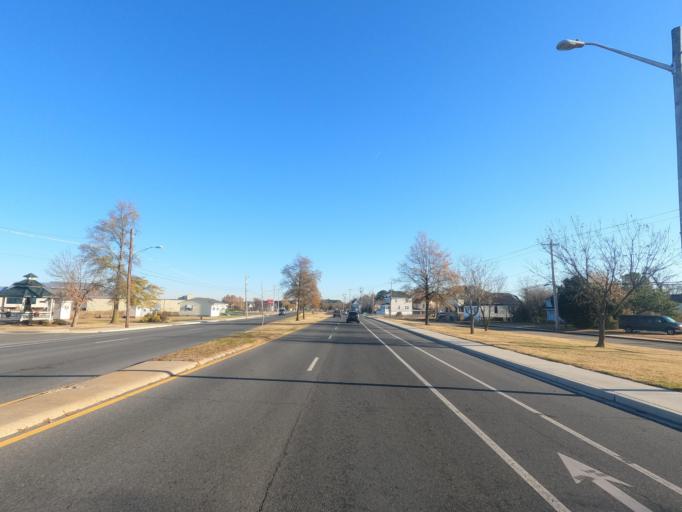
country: US
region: Maryland
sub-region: Somerset County
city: Crisfield
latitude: 37.9833
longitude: -75.8546
